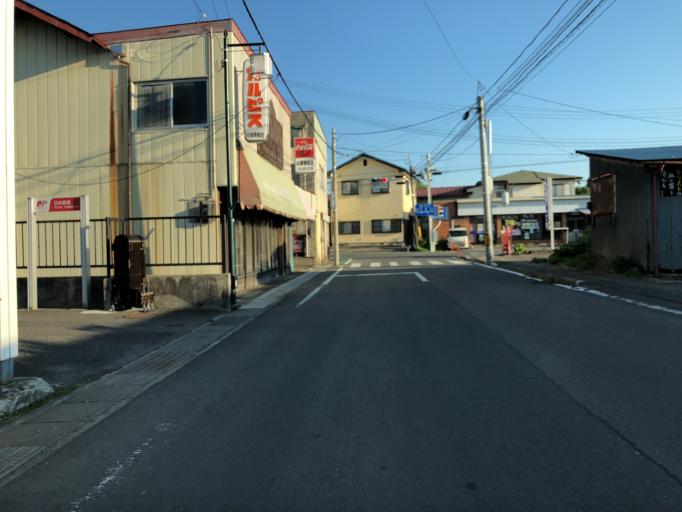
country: JP
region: Fukushima
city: Ishikawa
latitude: 37.0817
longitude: 140.4165
